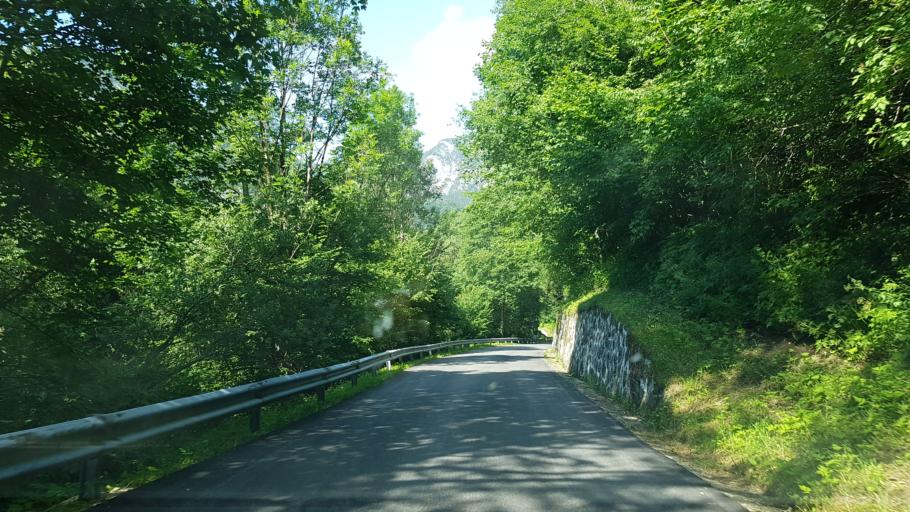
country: IT
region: Friuli Venezia Giulia
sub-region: Provincia di Udine
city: Pontebba
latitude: 46.5109
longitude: 13.2856
